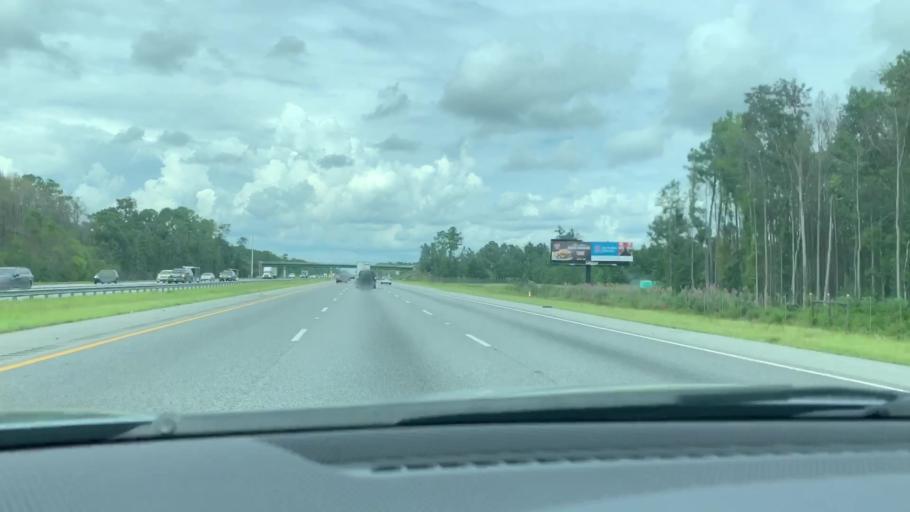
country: US
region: Georgia
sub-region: McIntosh County
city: Darien
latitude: 31.4892
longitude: -81.4468
